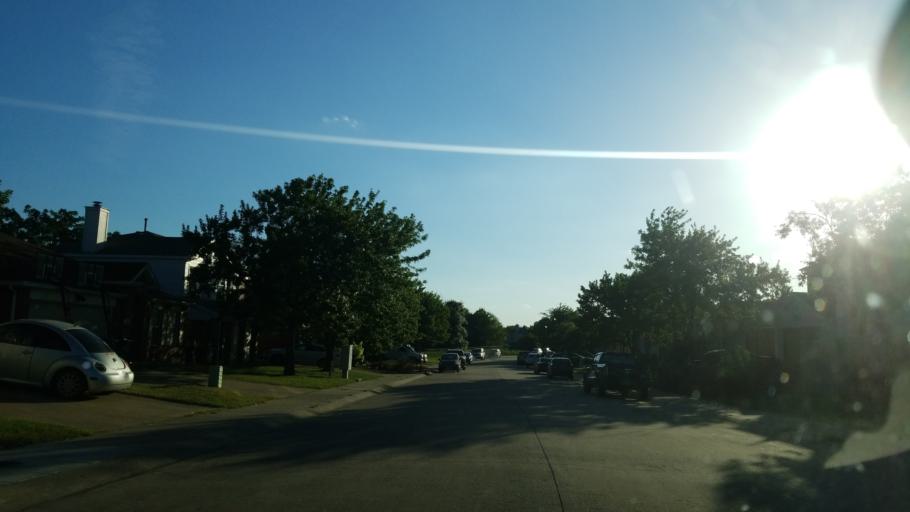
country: US
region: Texas
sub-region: Dallas County
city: Balch Springs
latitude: 32.7846
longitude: -96.6948
